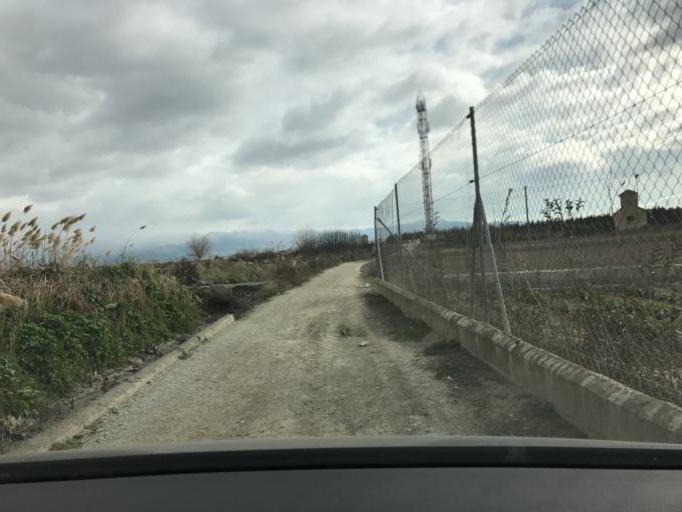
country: ES
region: Andalusia
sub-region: Provincia de Granada
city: Cullar-Vega
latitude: 37.1679
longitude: -3.6886
